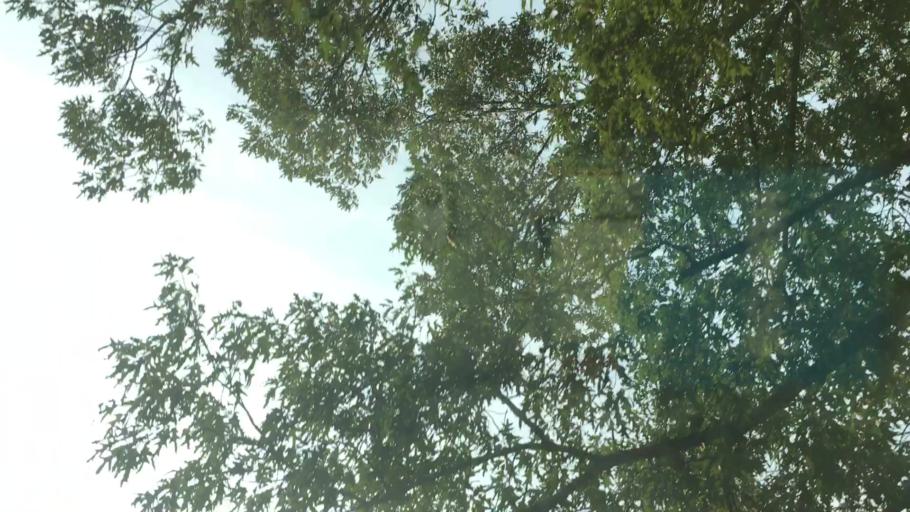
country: US
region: Alabama
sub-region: Bibb County
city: Woodstock
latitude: 33.2202
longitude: -87.1187
